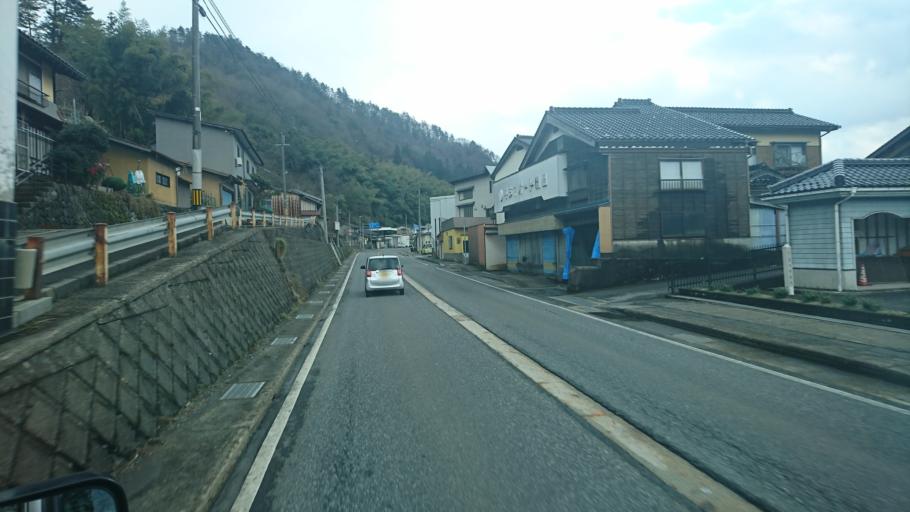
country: JP
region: Hyogo
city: Toyooka
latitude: 35.4723
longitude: 134.5962
